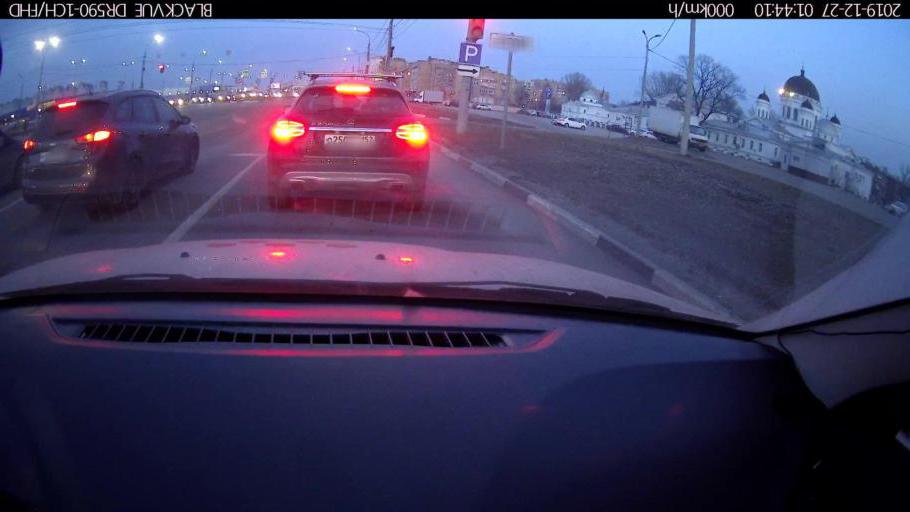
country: RU
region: Nizjnij Novgorod
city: Nizhniy Novgorod
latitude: 56.3315
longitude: 43.9514
